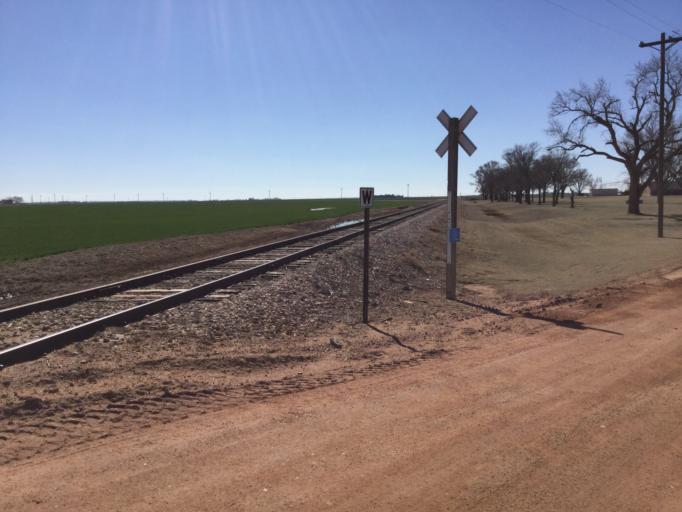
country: US
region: Kansas
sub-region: Barber County
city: Kiowa
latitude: 37.0019
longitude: -98.4854
